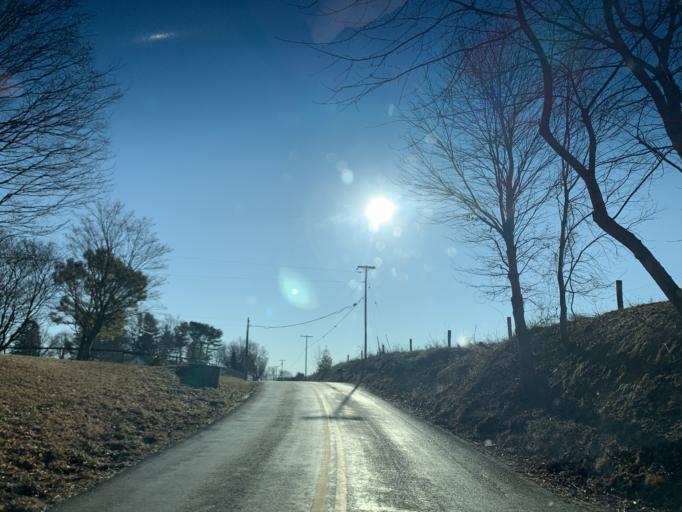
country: US
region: Maryland
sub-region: Harford County
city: Aberdeen
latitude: 39.5870
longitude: -76.2131
